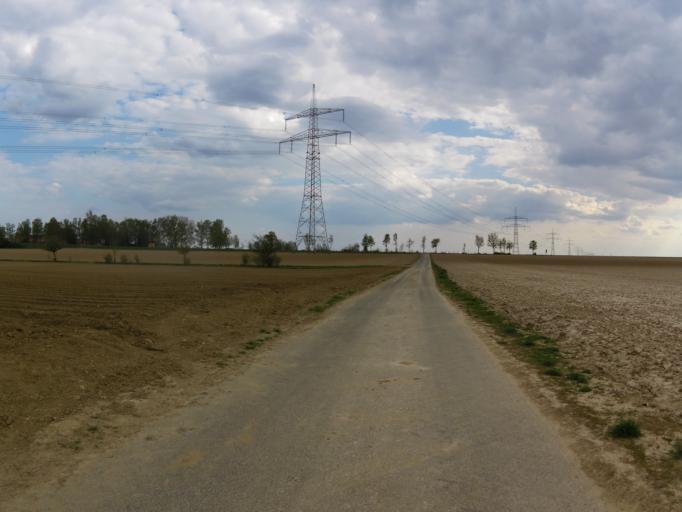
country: DE
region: Bavaria
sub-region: Regierungsbezirk Unterfranken
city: Oberpleichfeld
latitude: 49.8563
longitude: 10.0952
